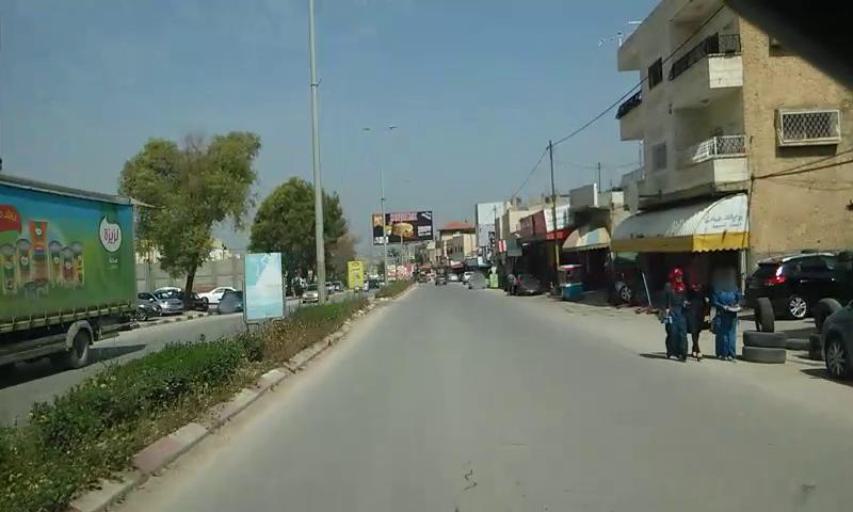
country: PS
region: West Bank
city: Janin
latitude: 32.4656
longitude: 35.3052
